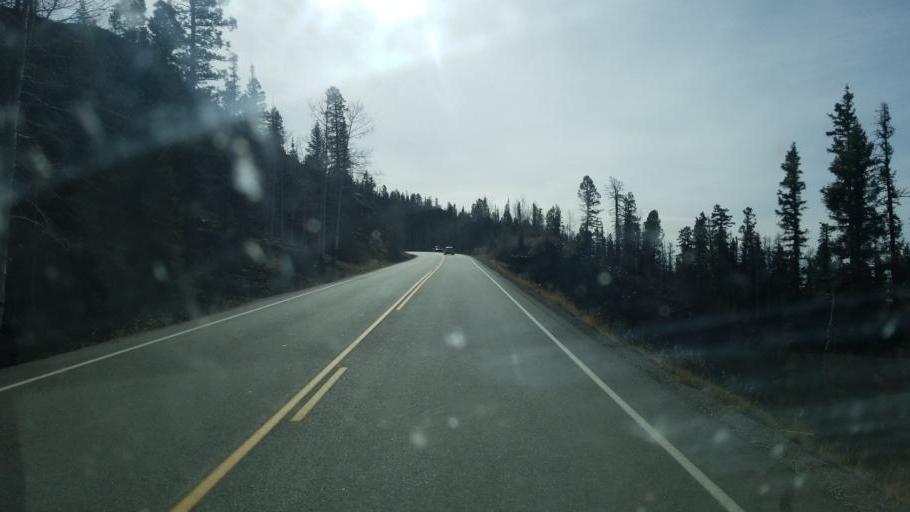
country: US
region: Colorado
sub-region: San Juan County
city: Silverton
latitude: 37.6793
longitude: -107.7849
